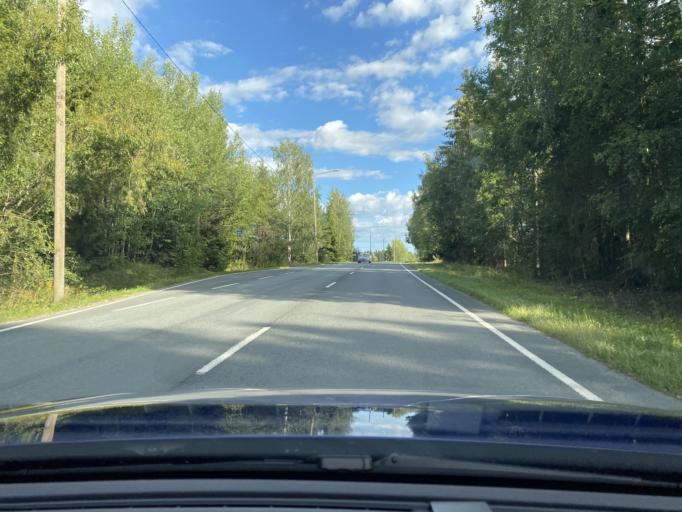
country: FI
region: Pirkanmaa
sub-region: Tampere
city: Lempaeaelae
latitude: 61.3772
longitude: 23.7821
